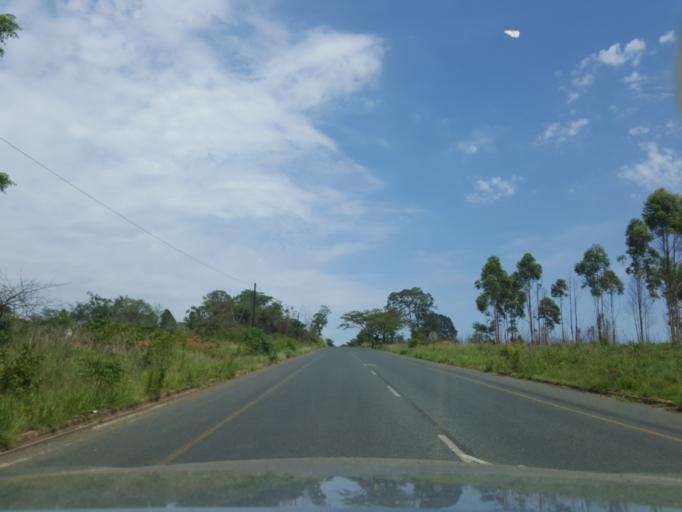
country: ZA
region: Mpumalanga
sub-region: Ehlanzeni District
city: White River
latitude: -25.3082
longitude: 31.0576
